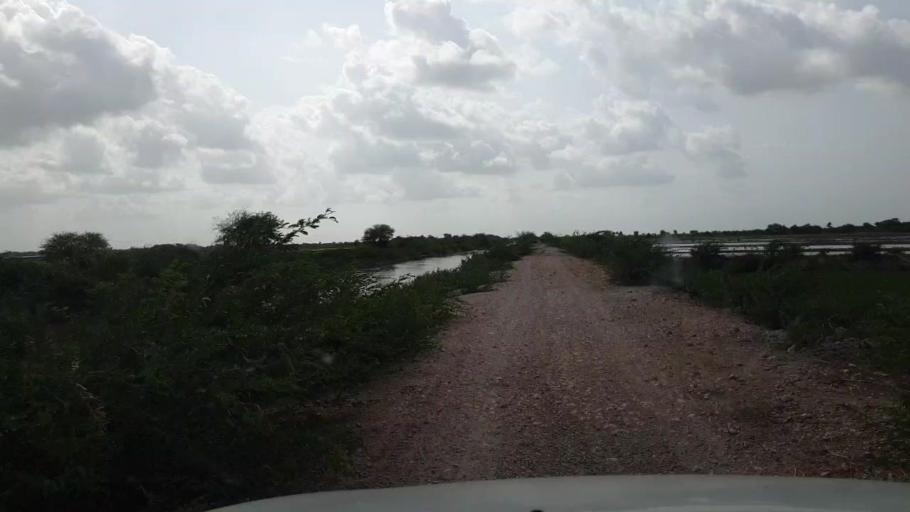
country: PK
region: Sindh
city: Kario
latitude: 24.7018
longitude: 68.6423
